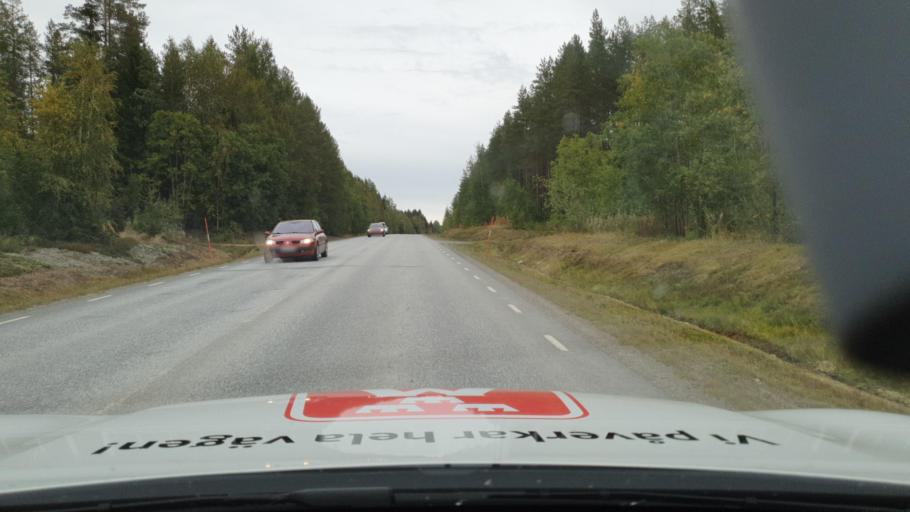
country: SE
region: Vaesterbotten
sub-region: Umea Kommun
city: Roback
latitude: 63.7802
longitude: 20.0757
